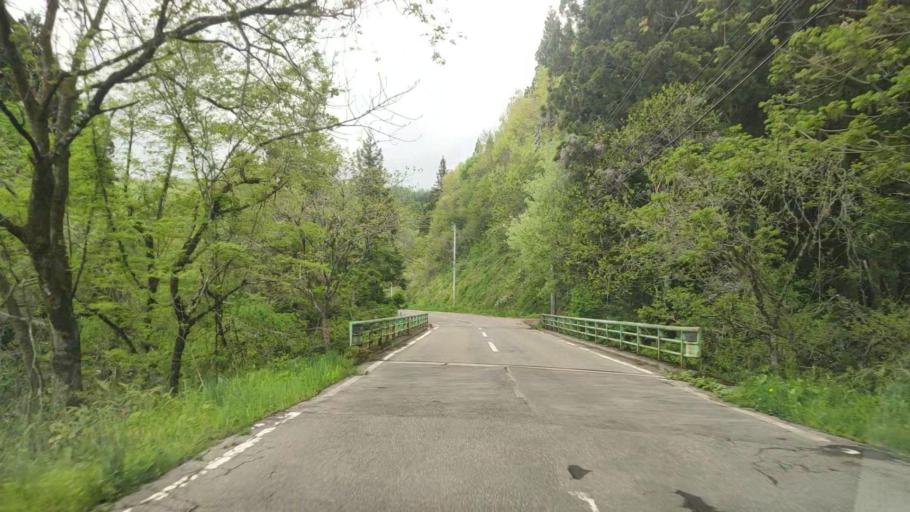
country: JP
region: Fukushima
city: Kitakata
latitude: 37.6585
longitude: 139.5901
